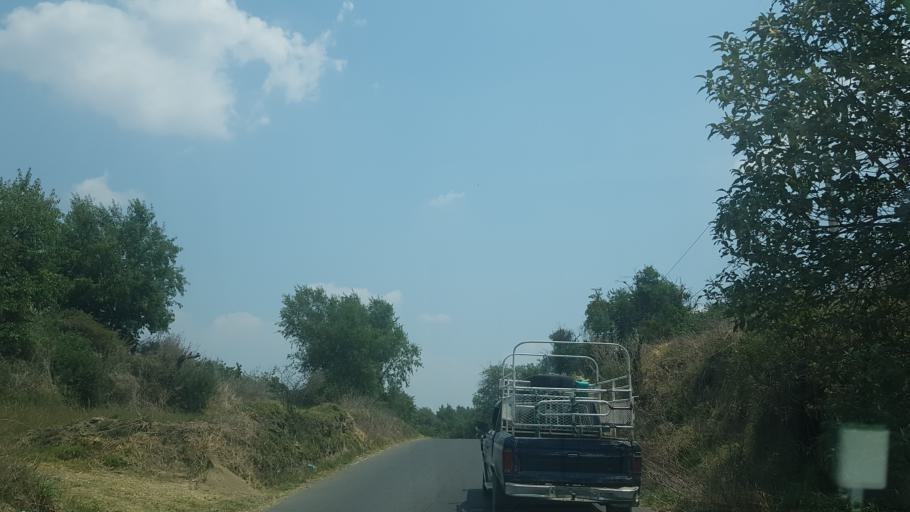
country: MX
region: Puebla
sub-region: San Nicolas de los Ranchos
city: San Pedro Yancuitlalpan
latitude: 19.0936
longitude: -98.4827
